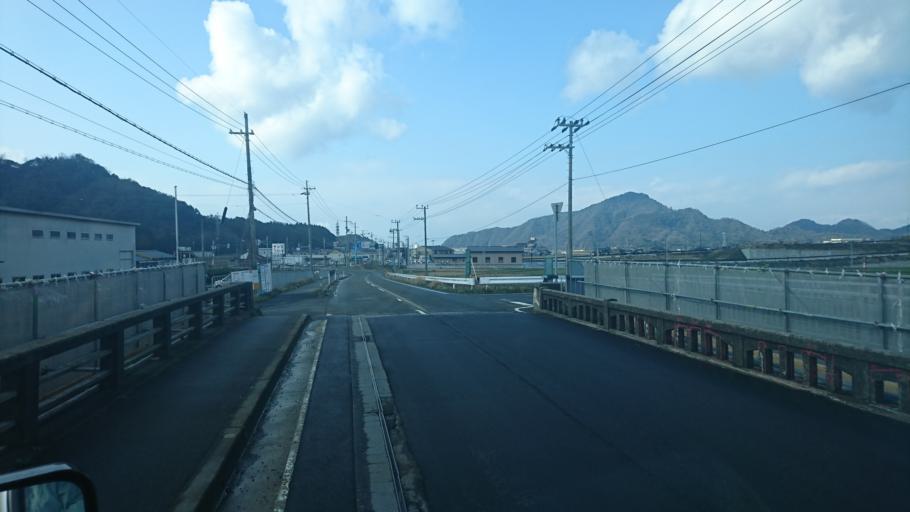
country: JP
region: Tottori
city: Tottori
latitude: 35.6094
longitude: 134.4715
